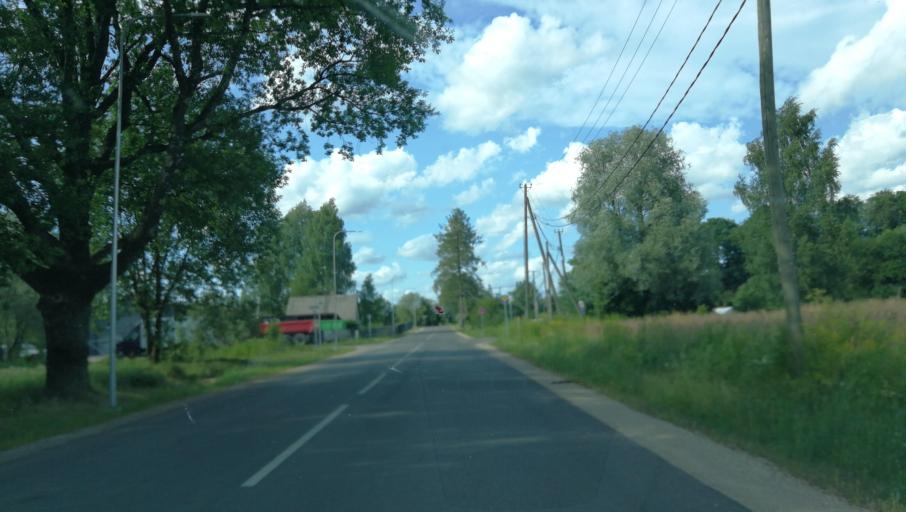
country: LV
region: Cesu Rajons
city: Cesis
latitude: 57.3206
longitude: 25.3096
